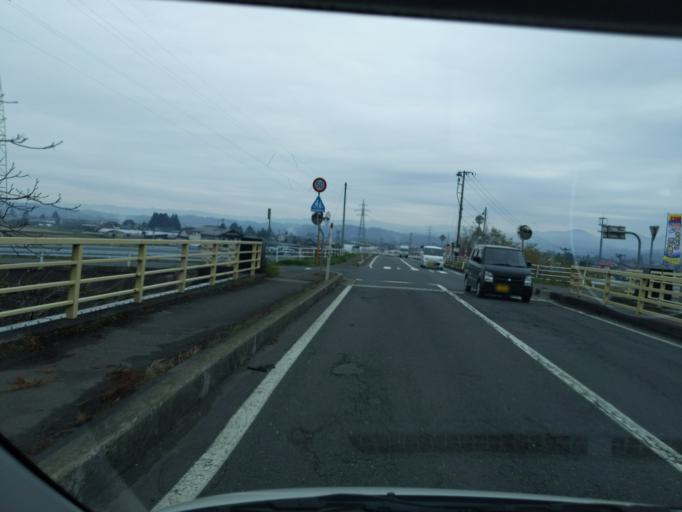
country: JP
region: Iwate
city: Mizusawa
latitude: 39.1563
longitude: 141.1699
